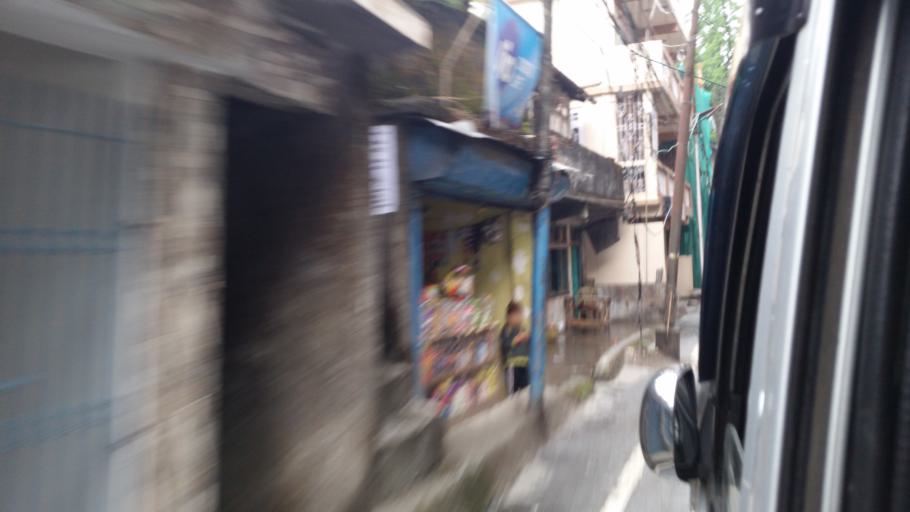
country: IN
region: West Bengal
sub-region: Darjiling
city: Darjiling
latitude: 27.0338
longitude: 88.2598
